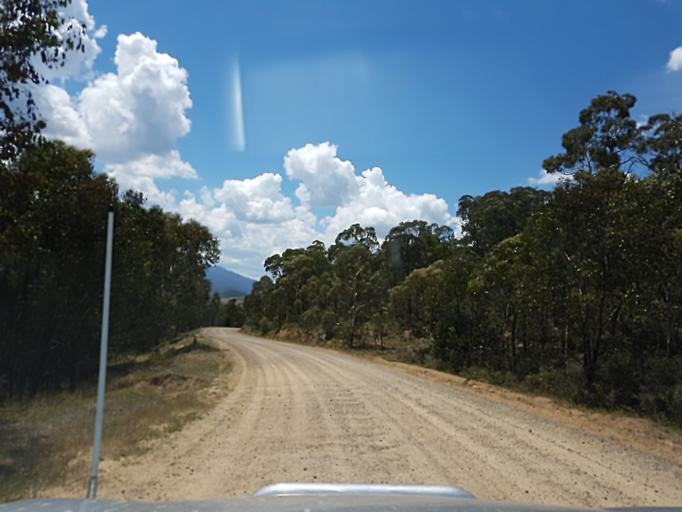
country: AU
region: Victoria
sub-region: Alpine
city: Mount Beauty
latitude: -36.9004
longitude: 147.8149
